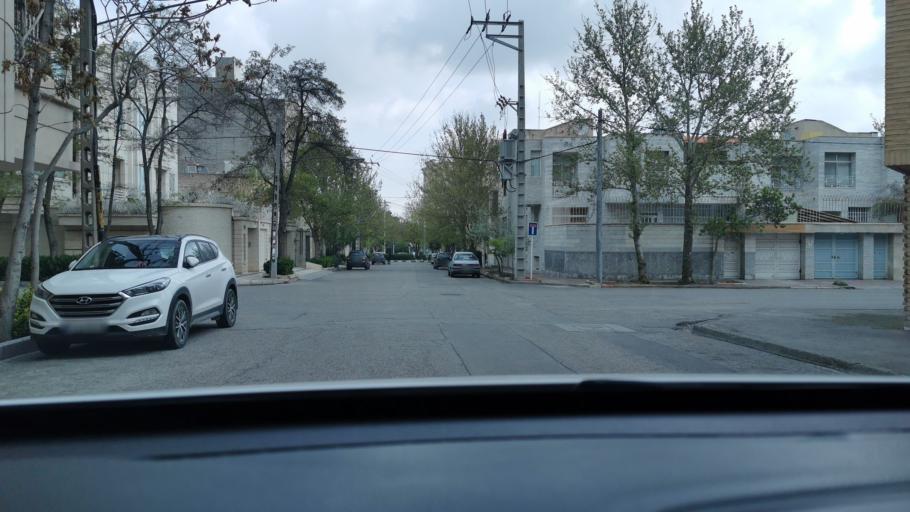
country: IR
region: Razavi Khorasan
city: Mashhad
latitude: 36.2917
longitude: 59.5611
